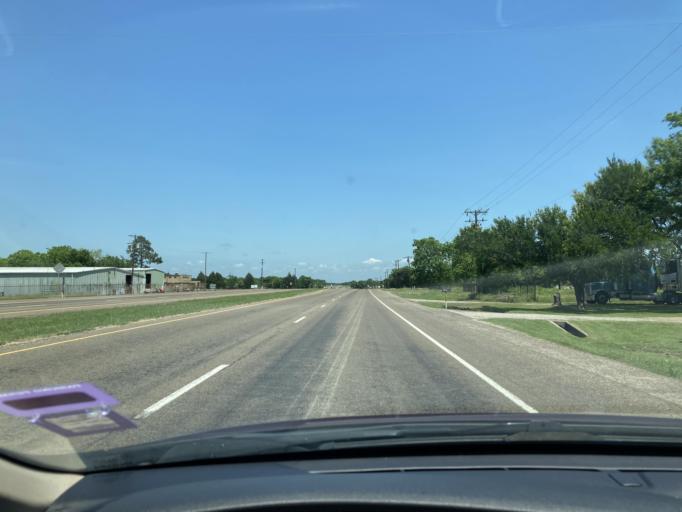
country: US
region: Texas
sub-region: Navarro County
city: Kerens
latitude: 32.1343
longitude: -96.2213
